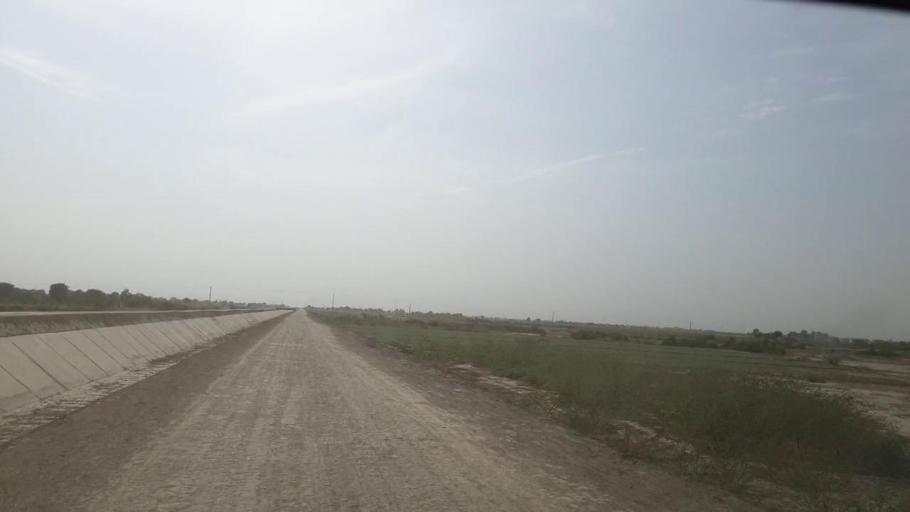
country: PK
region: Sindh
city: Nabisar
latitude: 25.0506
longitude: 69.5266
